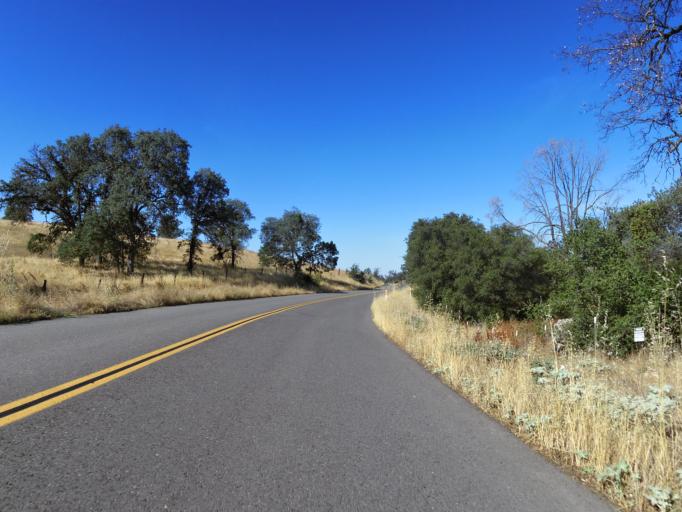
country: US
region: California
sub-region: Madera County
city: Yosemite Lakes
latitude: 37.1791
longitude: -119.8319
